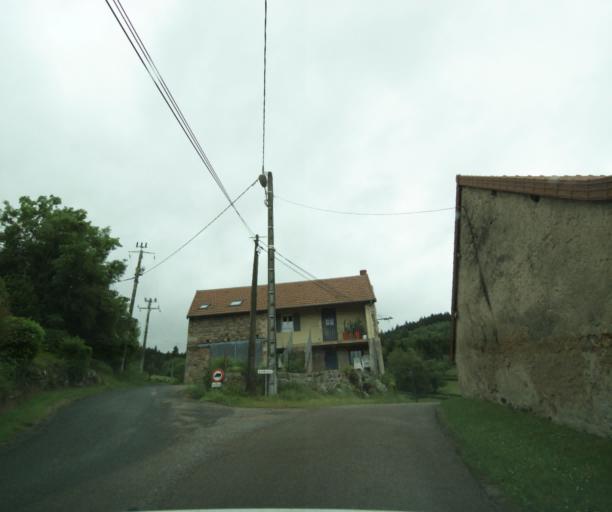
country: FR
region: Bourgogne
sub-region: Departement de Saone-et-Loire
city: Matour
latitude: 46.4314
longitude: 4.4620
